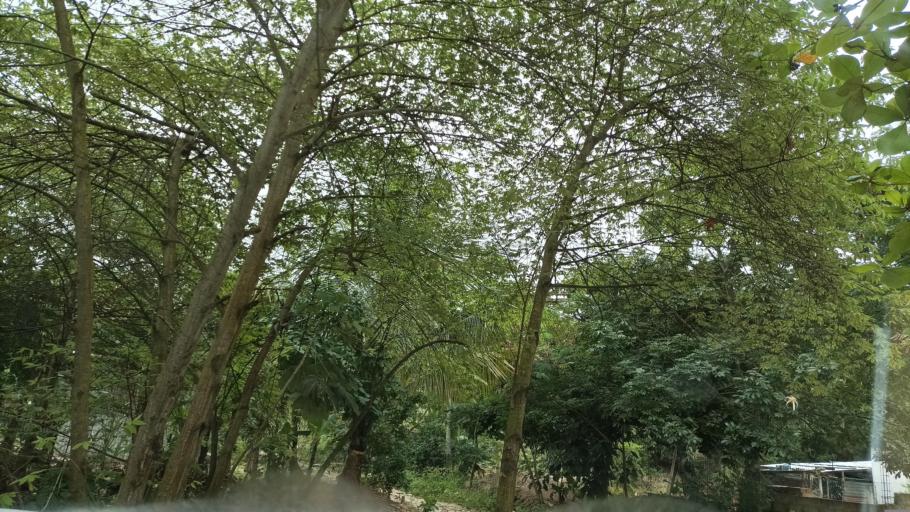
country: MX
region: Veracruz
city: Villa Nanchital
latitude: 18.0524
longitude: -94.4063
